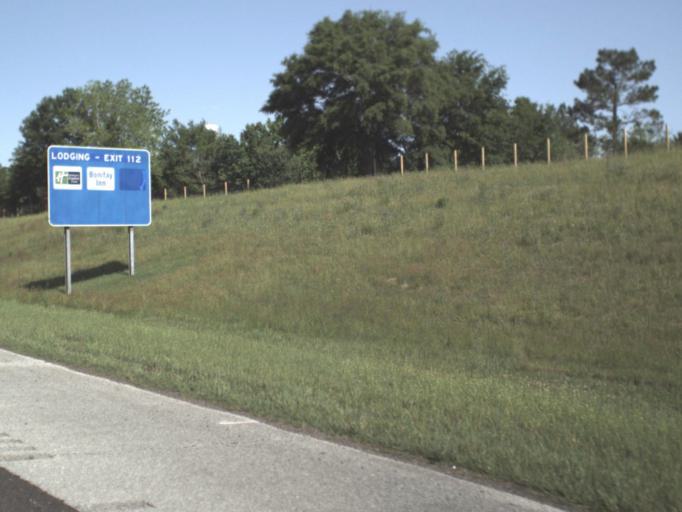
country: US
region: Florida
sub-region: Holmes County
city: Bonifay
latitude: 30.7624
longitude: -85.6689
